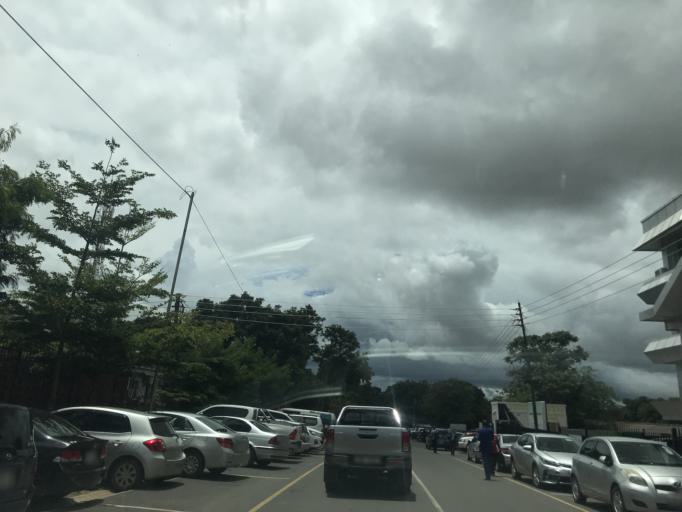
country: ZM
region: Lusaka
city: Lusaka
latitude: -15.4238
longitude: 28.3072
